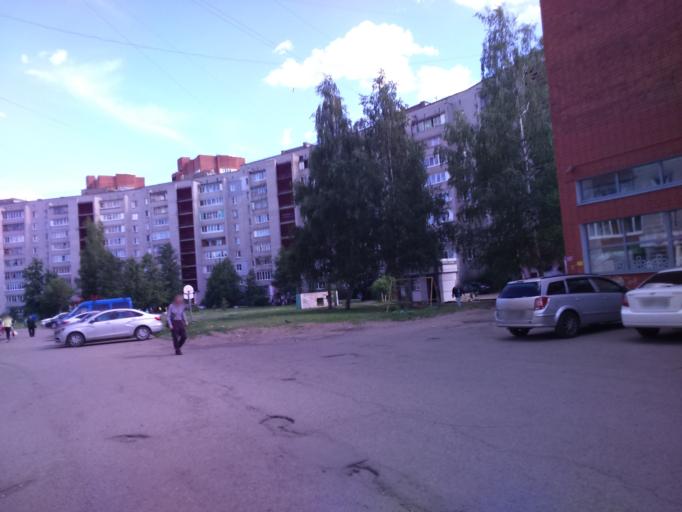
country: RU
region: Jaroslavl
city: Yaroslavl
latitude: 57.5713
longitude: 39.8606
